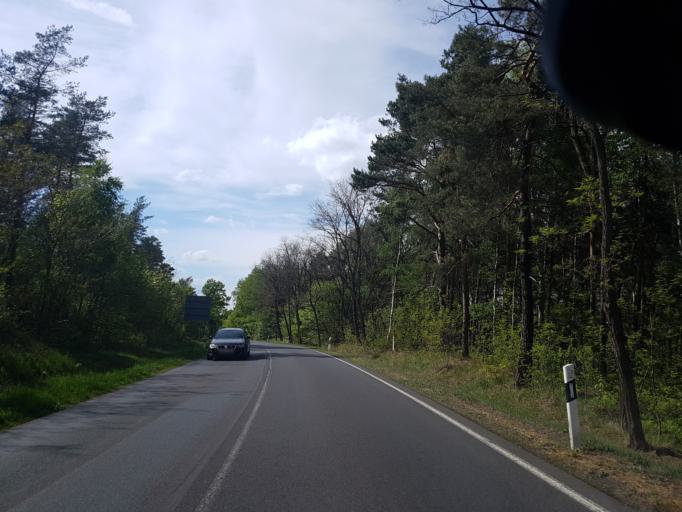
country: DE
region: Saxony
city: Gross Duben
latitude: 51.6312
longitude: 14.5725
